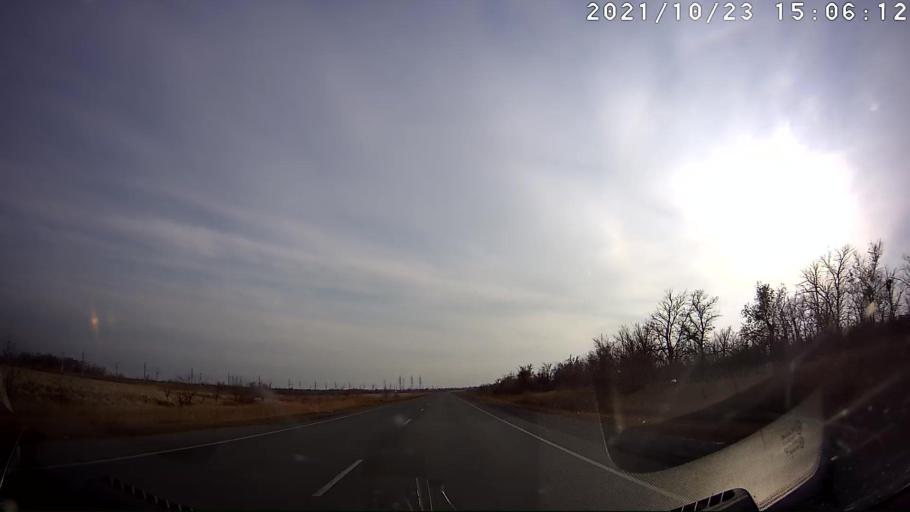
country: RU
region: Volgograd
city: Volgograd
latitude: 48.3734
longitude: 44.3585
